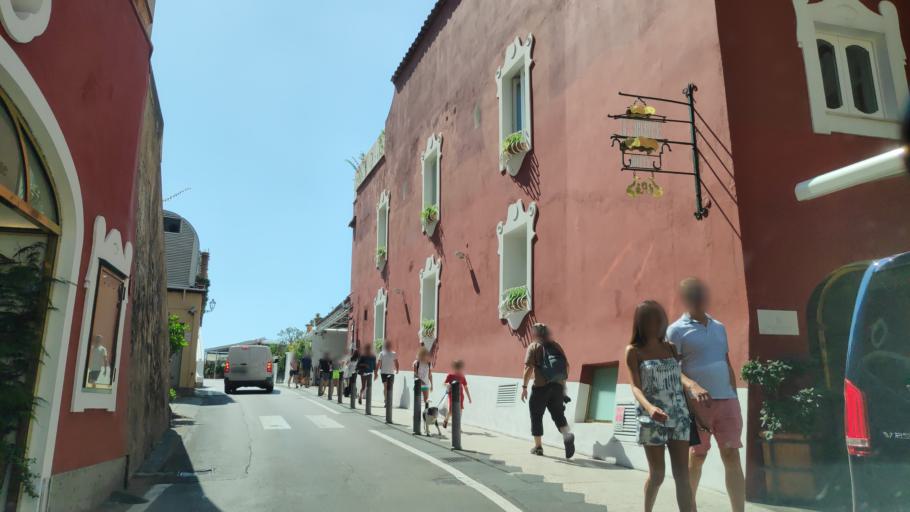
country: IT
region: Campania
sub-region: Provincia di Salerno
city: Positano
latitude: 40.6289
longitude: 14.4876
